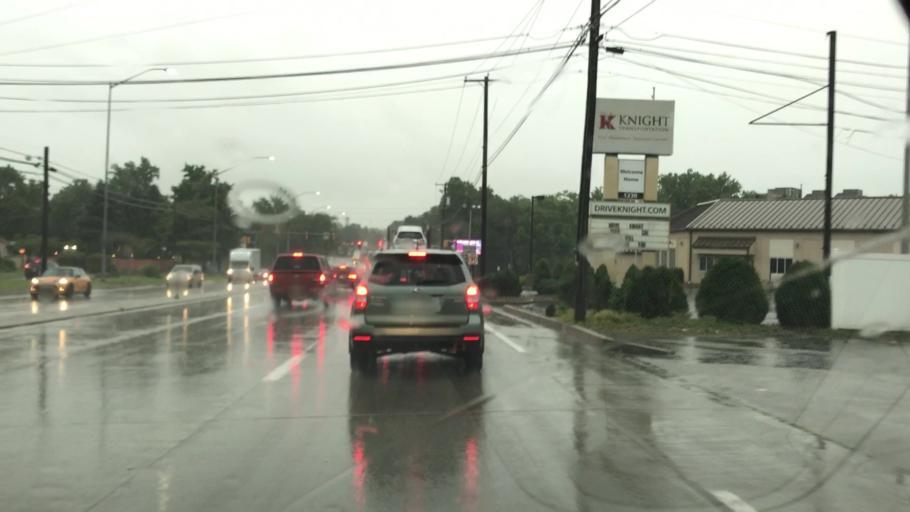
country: US
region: Pennsylvania
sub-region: Cumberland County
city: Schlusser
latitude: 40.2345
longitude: -77.1364
